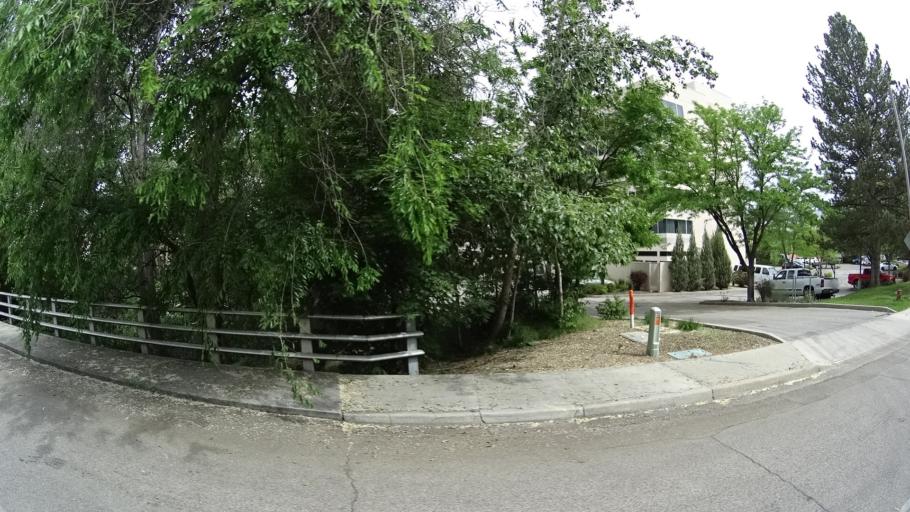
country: US
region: Idaho
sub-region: Ada County
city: Boise
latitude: 43.5972
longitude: -116.1866
